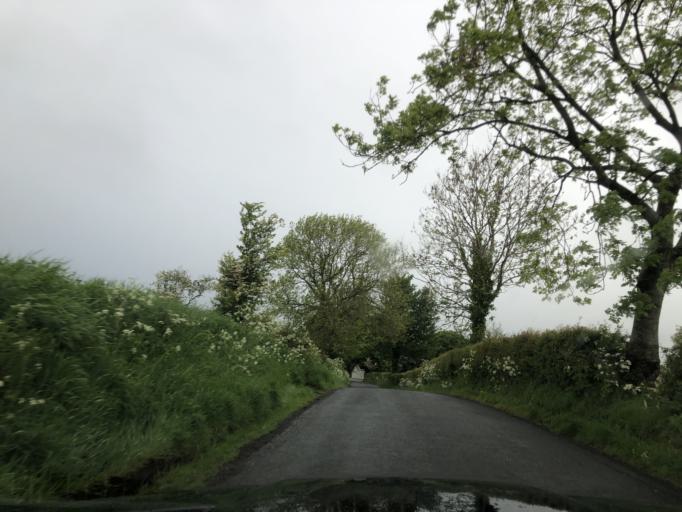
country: GB
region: Northern Ireland
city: Dunloy
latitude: 55.1389
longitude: -6.3762
